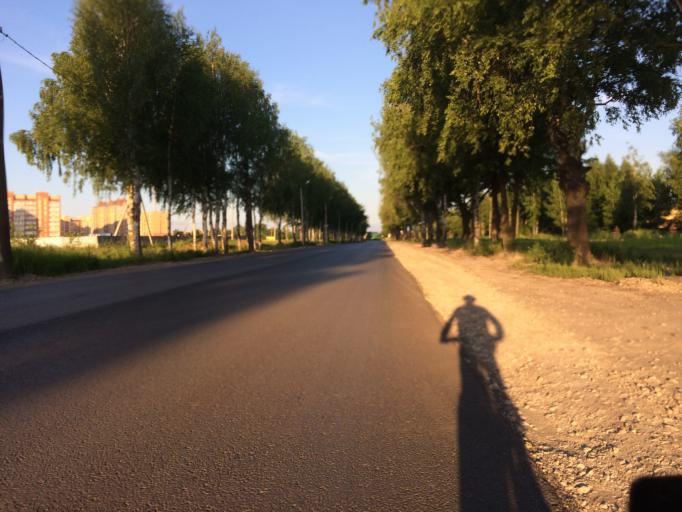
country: RU
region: Mariy-El
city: Medvedevo
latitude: 56.6521
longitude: 47.8365
